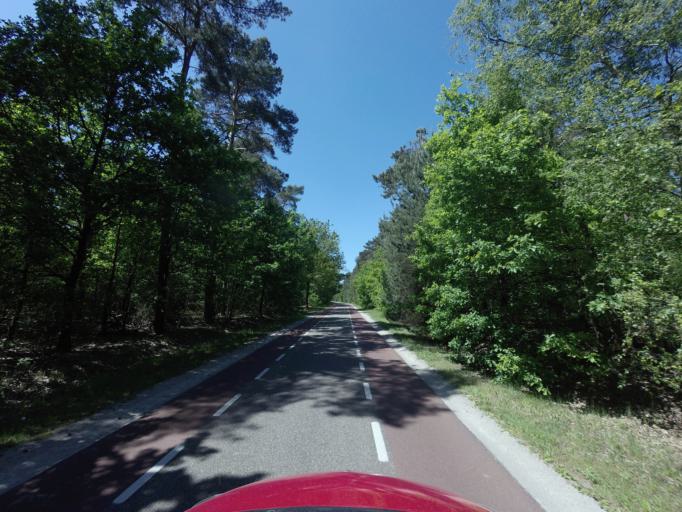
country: NL
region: North Brabant
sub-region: Gemeente Eersel
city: Eersel
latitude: 51.3082
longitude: 5.2872
